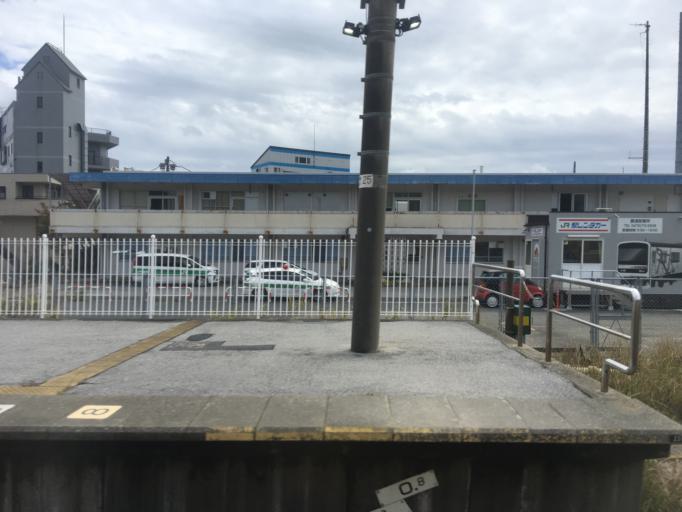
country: JP
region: Chiba
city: Katsuura
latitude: 35.1523
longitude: 140.3115
